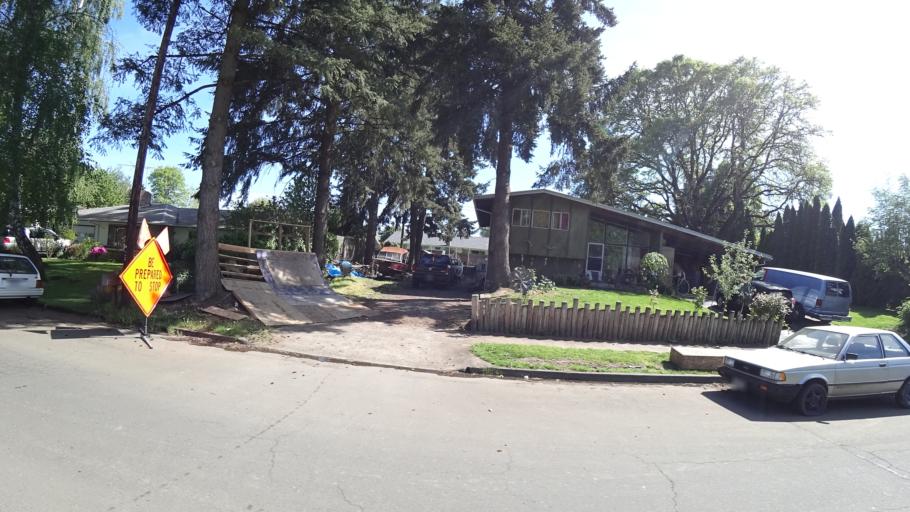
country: US
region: Oregon
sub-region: Washington County
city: Hillsboro
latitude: 45.5108
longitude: -122.9597
